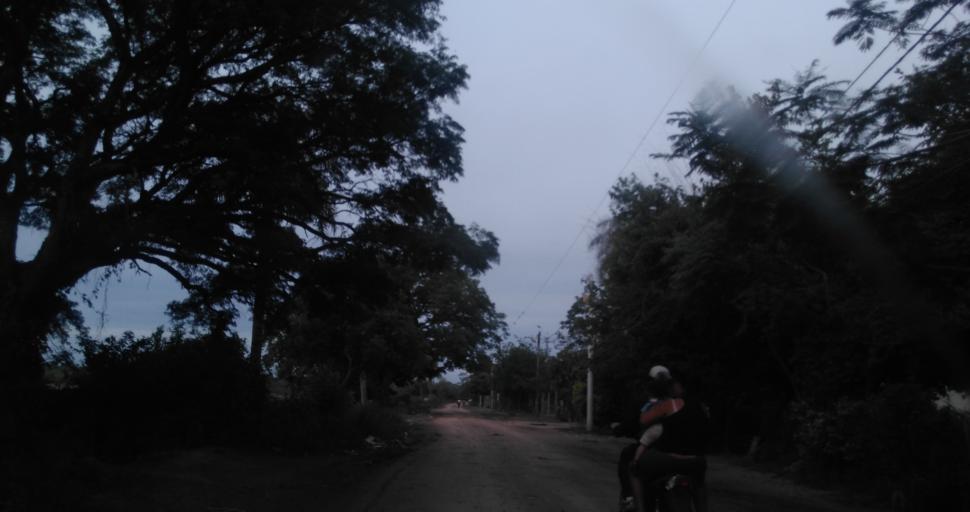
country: AR
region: Chaco
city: Fontana
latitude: -27.4076
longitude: -59.0259
